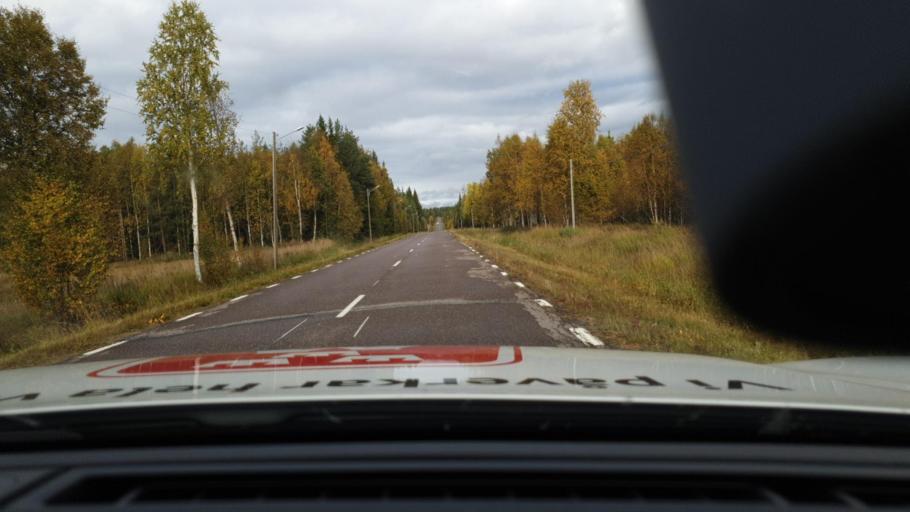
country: SE
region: Norrbotten
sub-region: Overkalix Kommun
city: OEverkalix
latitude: 67.0039
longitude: 22.5083
